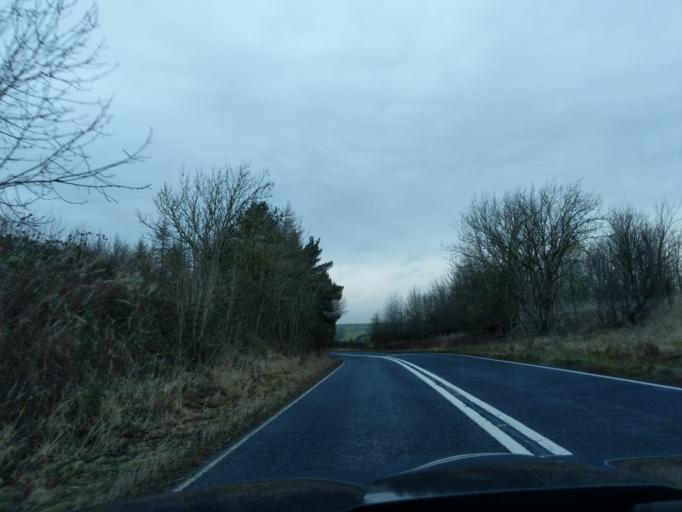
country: GB
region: England
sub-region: Northumberland
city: Rothley
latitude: 55.1454
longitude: -1.9924
